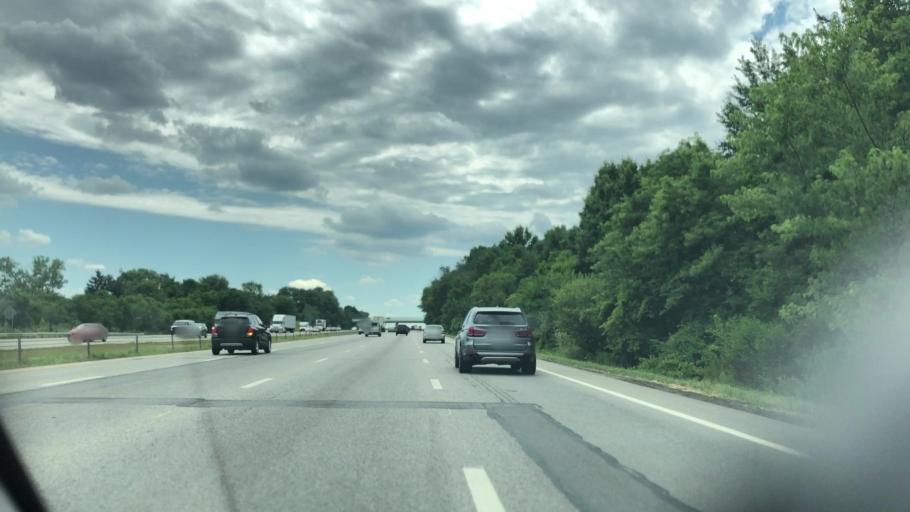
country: US
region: Ohio
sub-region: Summit County
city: Portage Lakes
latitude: 41.0029
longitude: -81.4942
